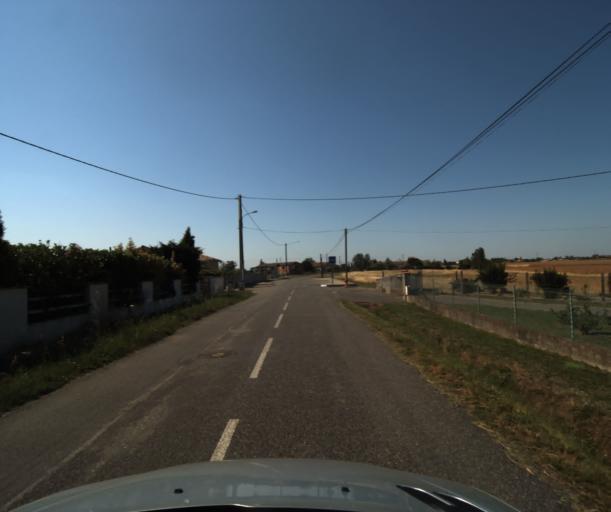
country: FR
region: Midi-Pyrenees
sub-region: Departement de la Haute-Garonne
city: Labarthe-sur-Leze
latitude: 43.4609
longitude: 1.3801
